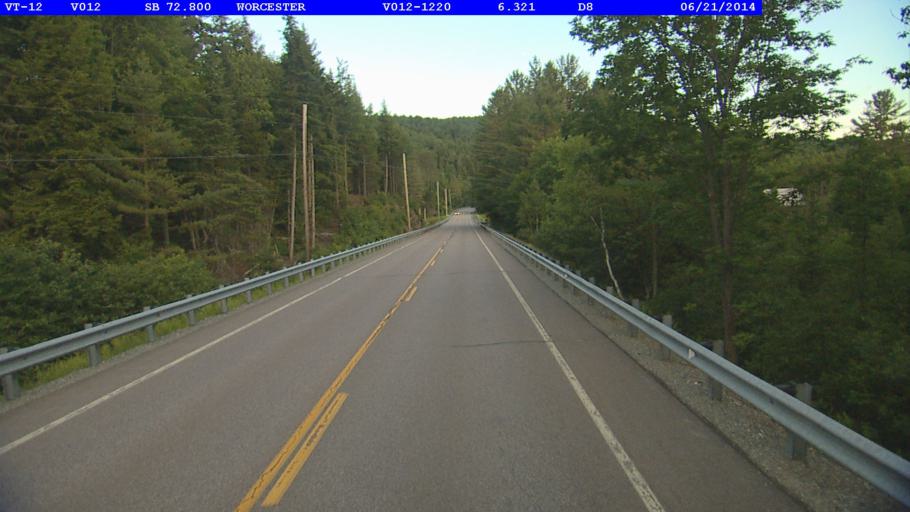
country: US
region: Vermont
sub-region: Lamoille County
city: Morrisville
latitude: 44.4325
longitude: -72.5345
